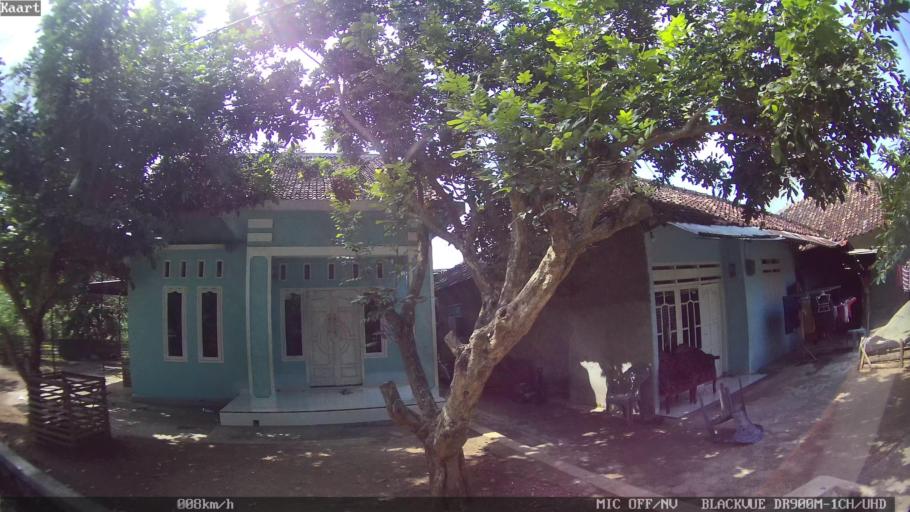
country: ID
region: Lampung
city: Kedaton
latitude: -5.3390
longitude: 105.2725
